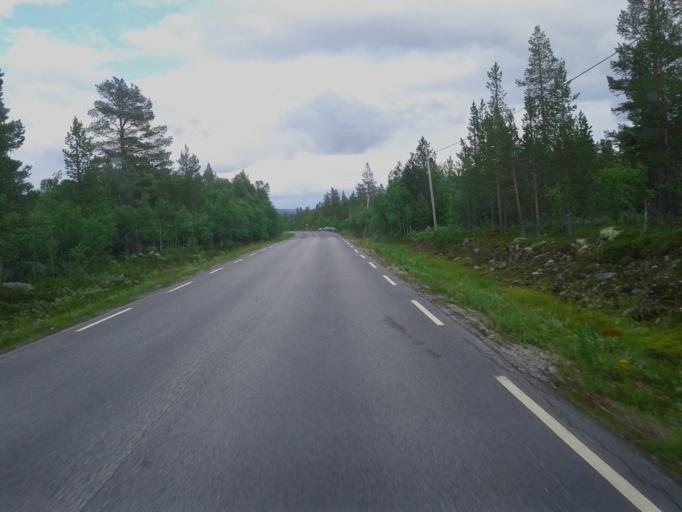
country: NO
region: Sor-Trondelag
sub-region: Roros
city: Roros
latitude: 62.3103
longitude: 11.6764
